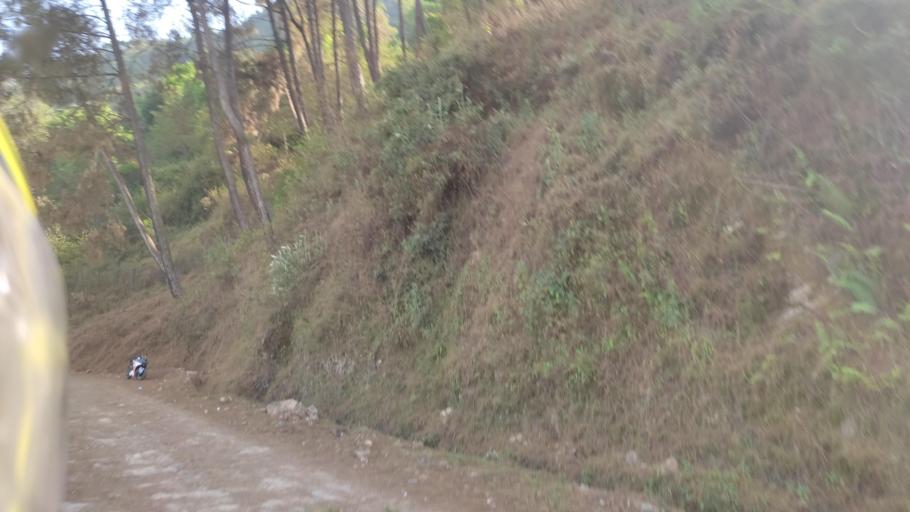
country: NP
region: Central Region
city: Kirtipur
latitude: 27.6583
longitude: 85.2644
